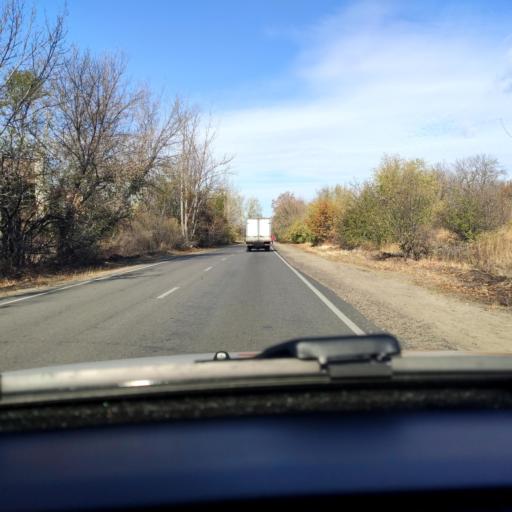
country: RU
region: Voronezj
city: Shilovo
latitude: 51.5671
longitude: 39.1399
